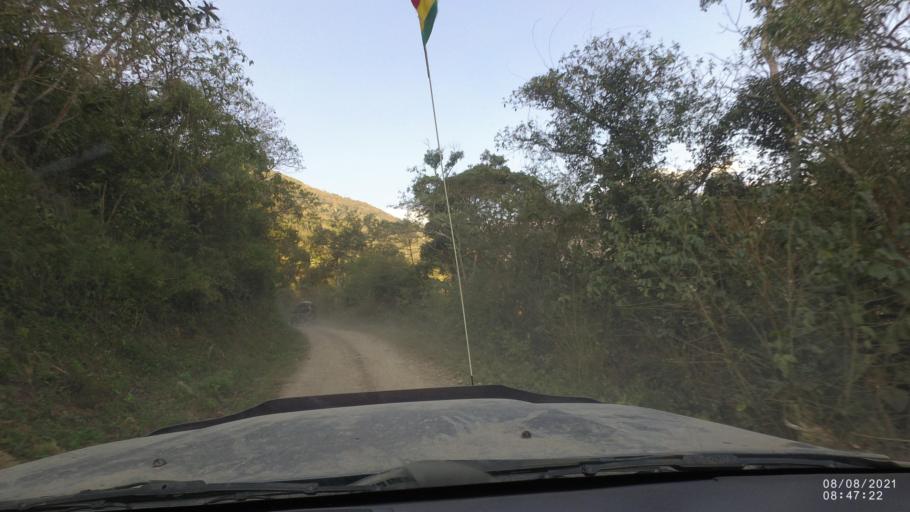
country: BO
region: La Paz
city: Quime
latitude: -16.5285
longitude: -66.7540
